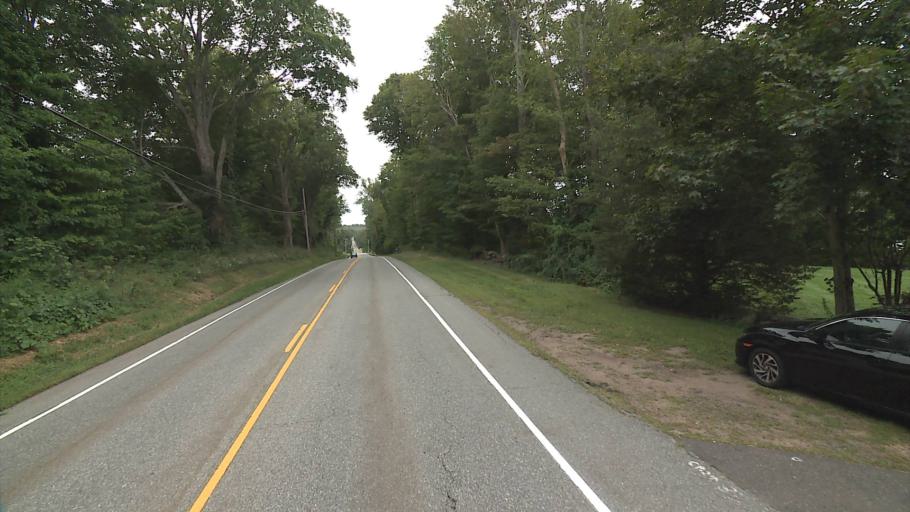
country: US
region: Connecticut
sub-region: Hartford County
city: Terramuggus
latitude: 41.7015
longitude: -72.4352
